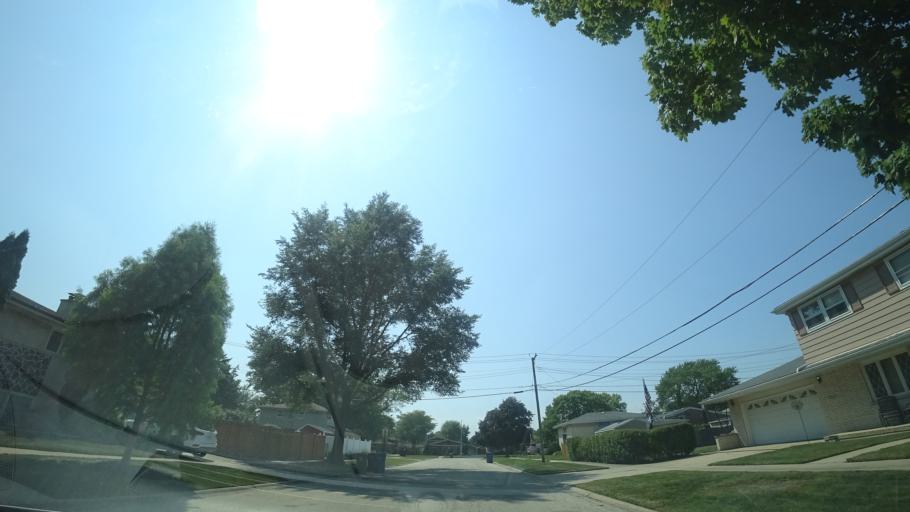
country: US
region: Illinois
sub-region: Cook County
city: Oak Lawn
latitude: 41.6964
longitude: -87.7437
